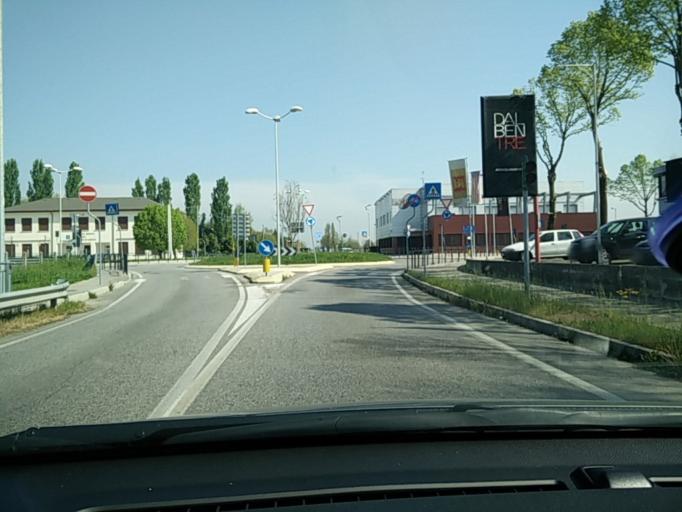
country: IT
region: Veneto
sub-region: Provincia di Treviso
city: Fornaci
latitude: 45.6639
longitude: 12.4348
